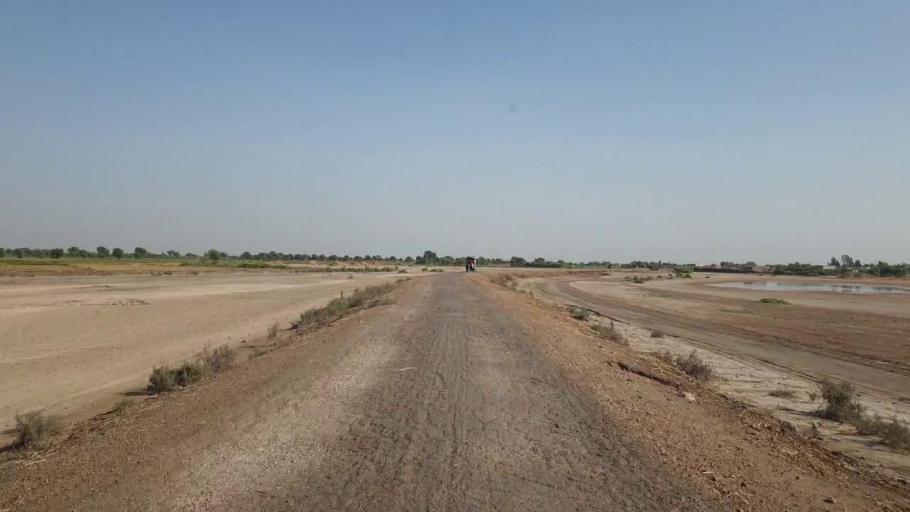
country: PK
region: Sindh
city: Matli
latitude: 25.0417
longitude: 68.7241
